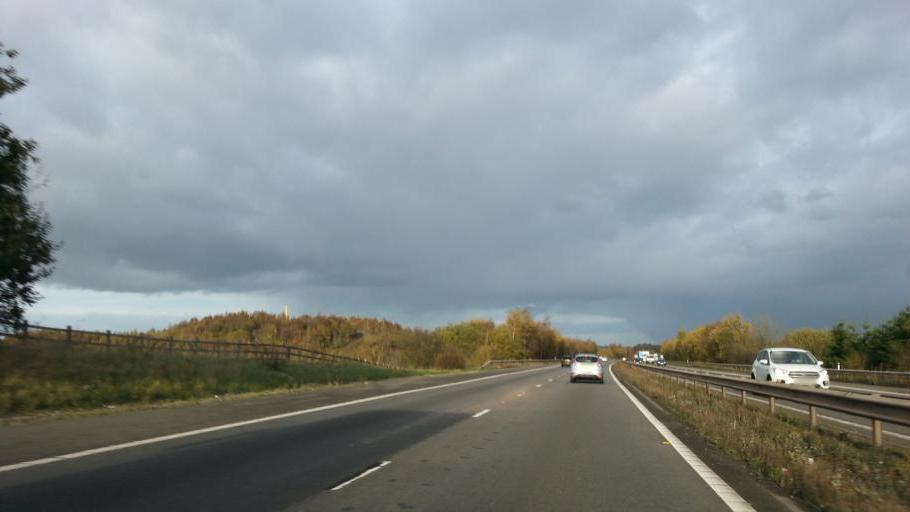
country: GB
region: England
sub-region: Staffordshire
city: Tamworth
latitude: 52.6260
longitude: -1.6237
